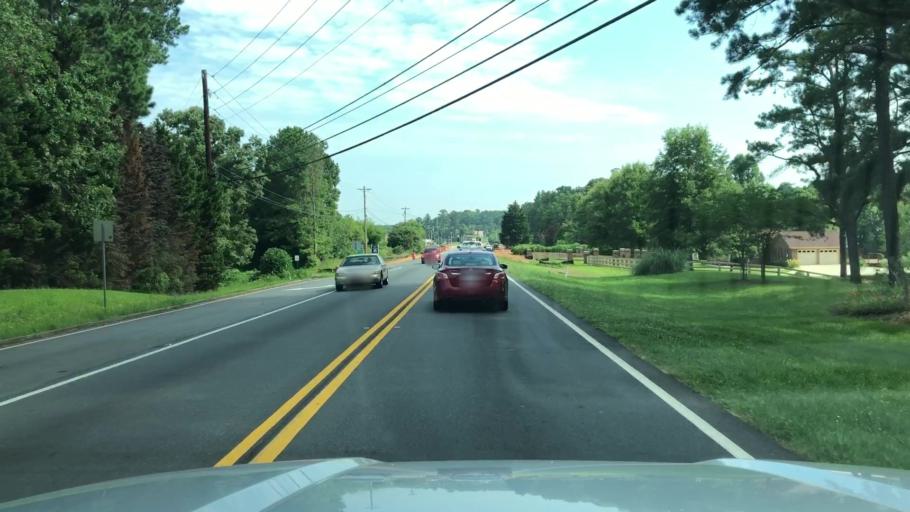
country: US
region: Georgia
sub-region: Cobb County
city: Acworth
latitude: 34.0559
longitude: -84.7229
